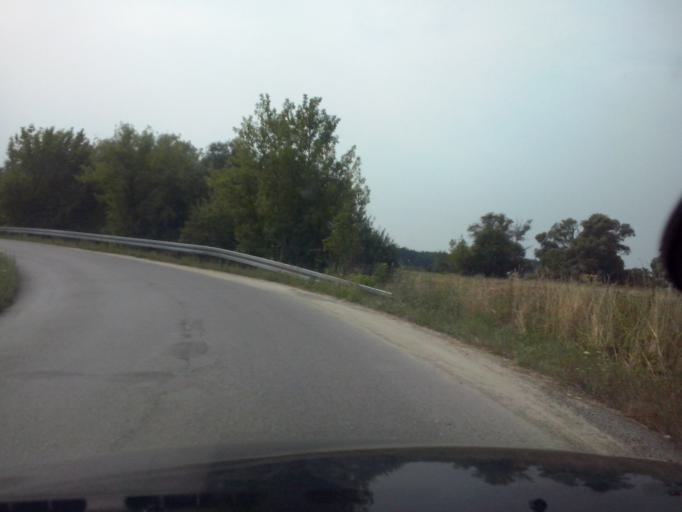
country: PL
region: Swietokrzyskie
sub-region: Powiat kielecki
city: Brzeziny
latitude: 50.7577
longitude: 20.5246
